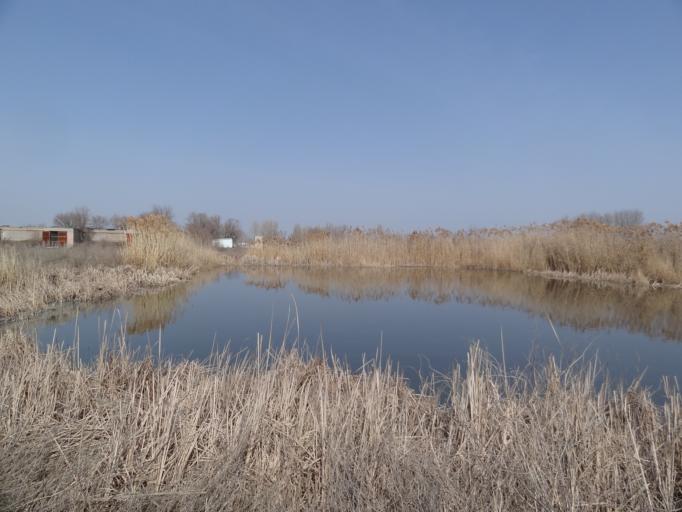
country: RU
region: Saratov
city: Engel's
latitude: 51.4228
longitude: 46.1781
